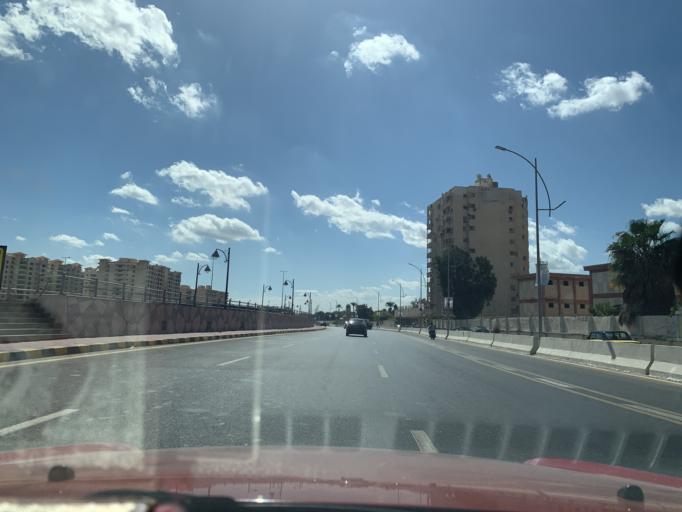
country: EG
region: Alexandria
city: Alexandria
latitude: 31.2061
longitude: 29.9545
